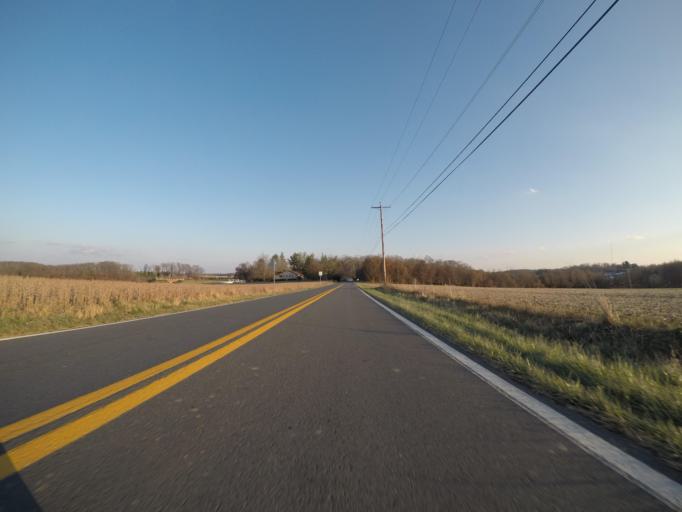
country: US
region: Maryland
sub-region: Carroll County
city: Hampstead
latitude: 39.5871
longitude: -76.8355
